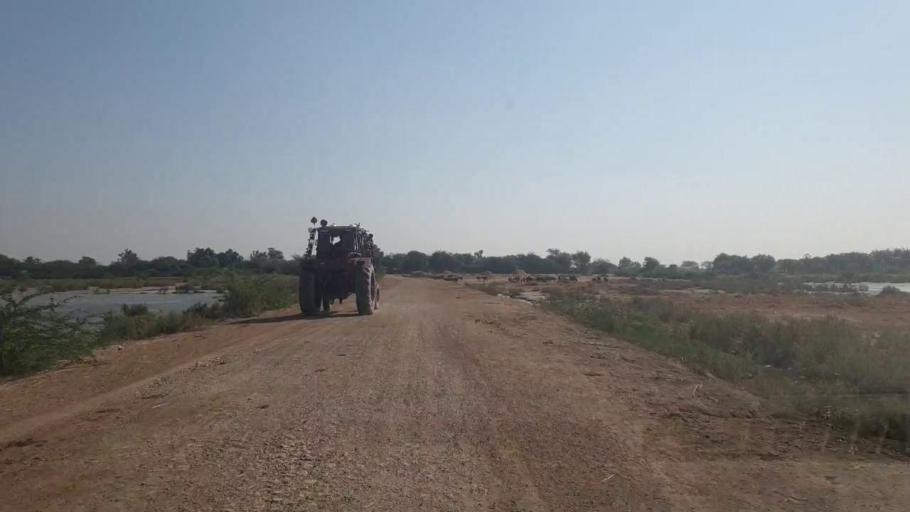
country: PK
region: Sindh
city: Badin
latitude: 24.5531
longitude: 68.8467
